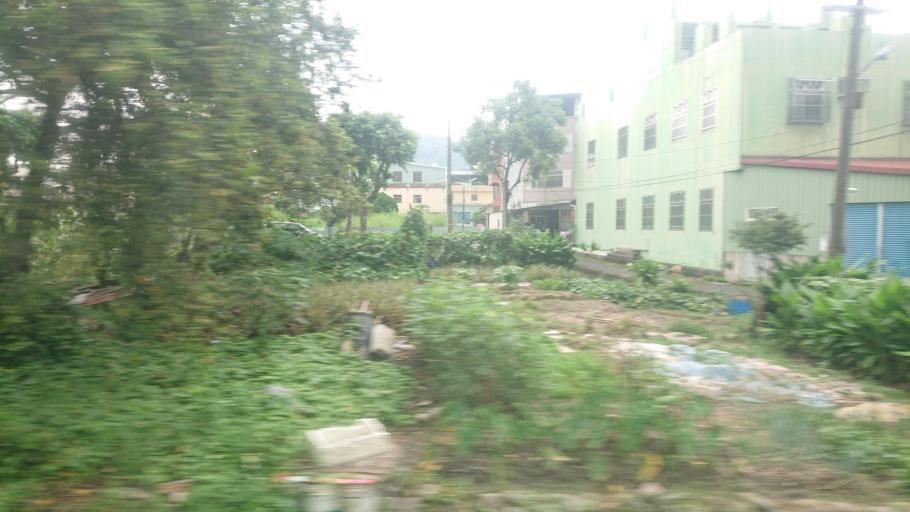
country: TW
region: Taiwan
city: Lugu
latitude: 23.8265
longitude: 120.7804
